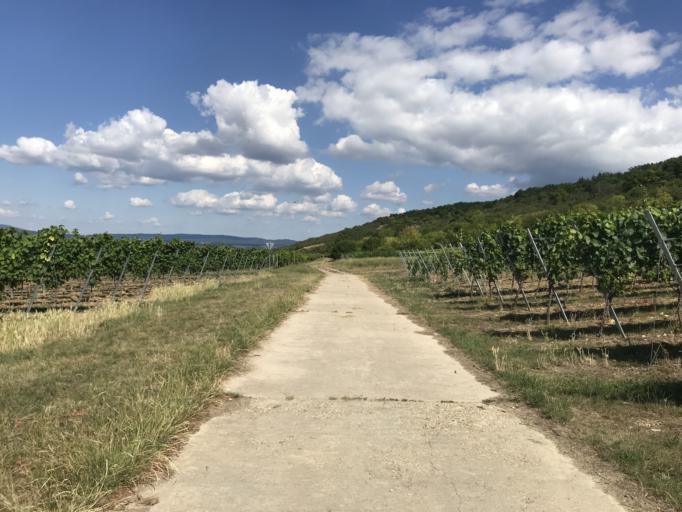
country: DE
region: Rheinland-Pfalz
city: Appenheim
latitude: 49.9406
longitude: 8.0351
